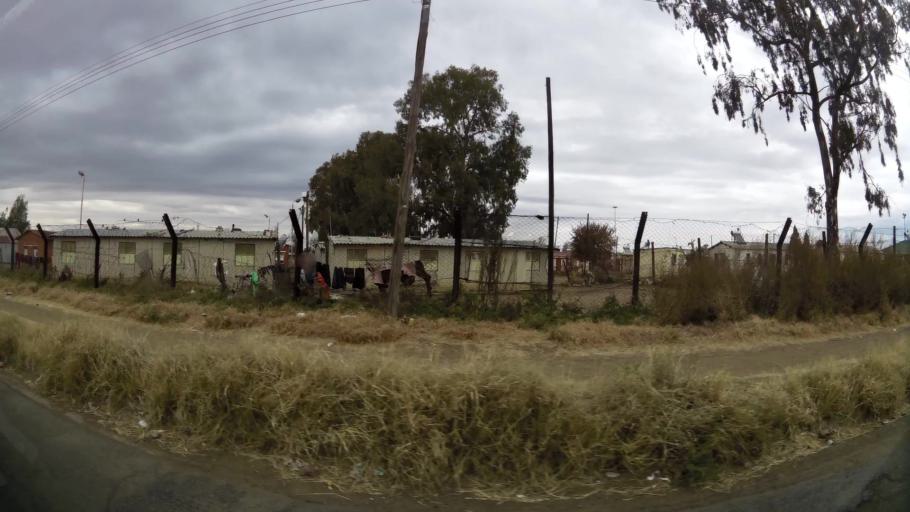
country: ZA
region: Orange Free State
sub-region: Fezile Dabi District Municipality
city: Kroonstad
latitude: -27.6524
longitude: 27.2116
